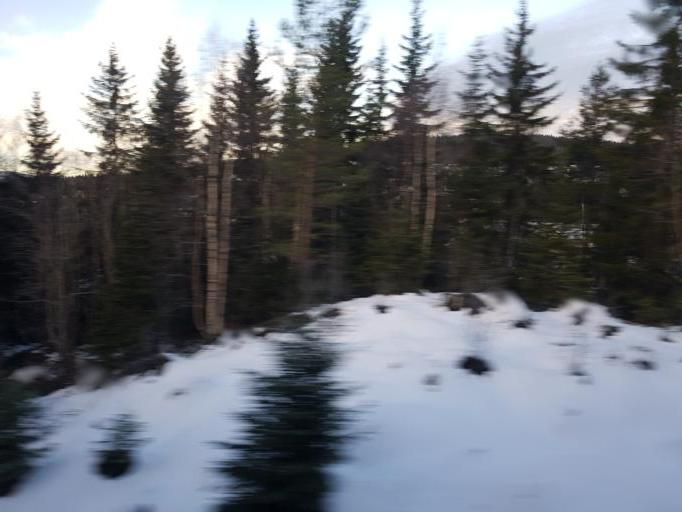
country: NO
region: Sor-Trondelag
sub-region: Rennebu
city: Berkak
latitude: 62.8339
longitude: 10.0129
